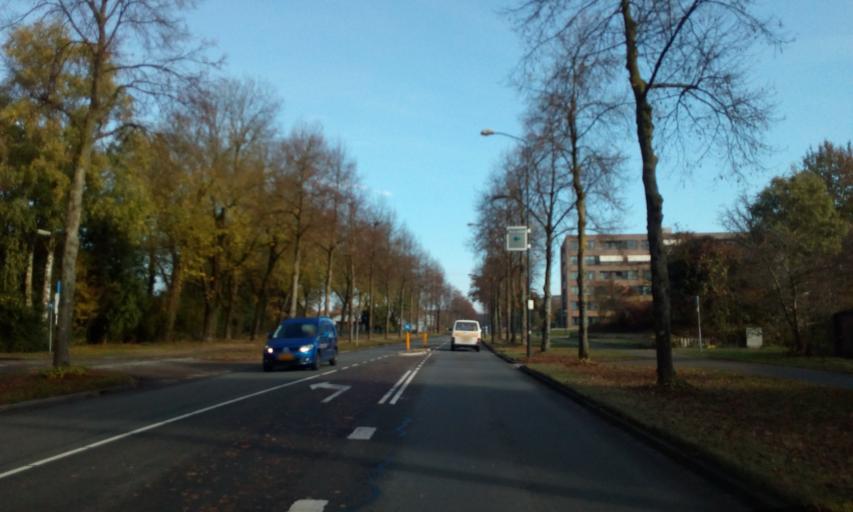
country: NL
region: Gelderland
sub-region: Gemeente Apeldoorn
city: Apeldoorn
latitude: 52.2025
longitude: 5.9511
